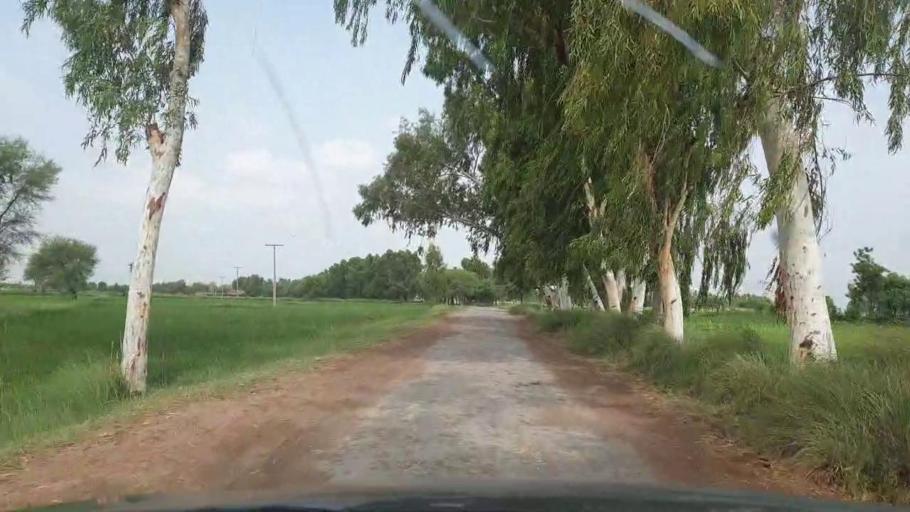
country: PK
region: Sindh
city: Ratodero
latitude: 27.8573
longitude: 68.2966
